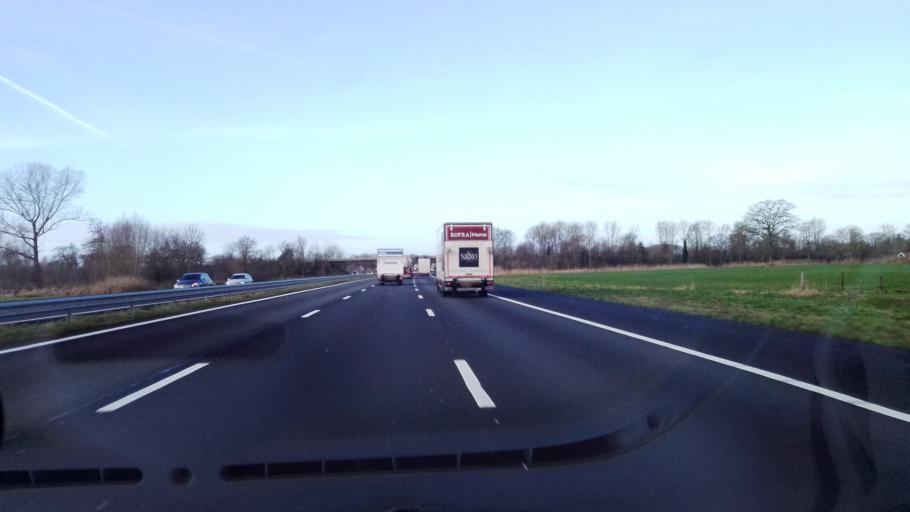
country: NL
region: Overijssel
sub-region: Gemeente Hof van Twente
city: Goor
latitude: 52.2846
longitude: 6.5926
